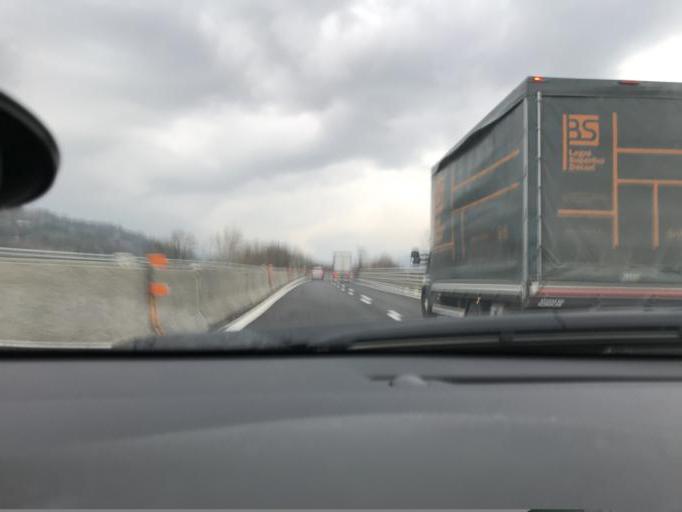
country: IT
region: The Marches
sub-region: Provincia di Ancona
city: Macine-Borgo Loreto
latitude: 43.4851
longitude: 13.0962
